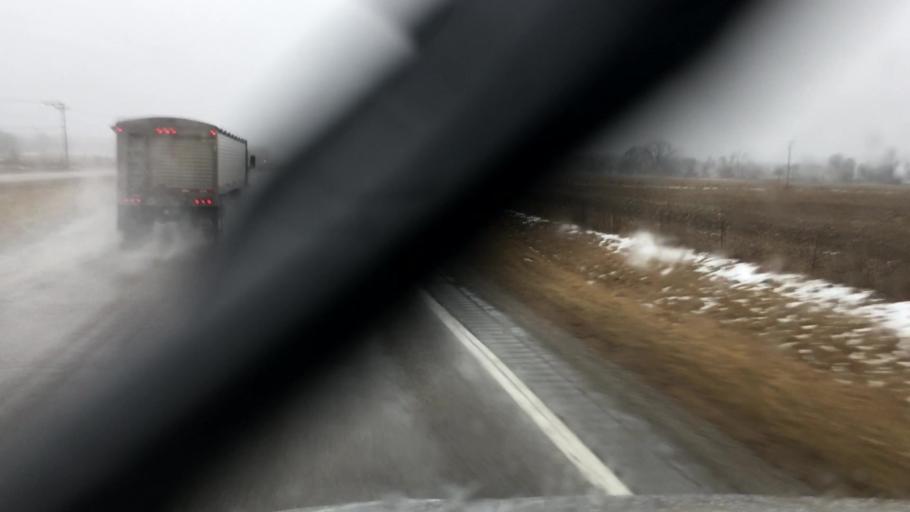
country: US
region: Indiana
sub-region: Newton County
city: Roselawn
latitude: 41.1173
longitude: -87.4489
